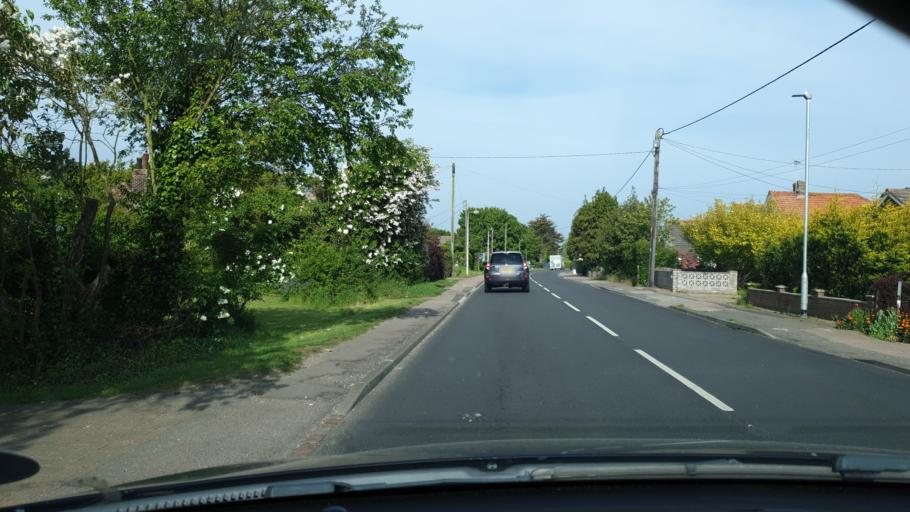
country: GB
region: England
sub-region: Essex
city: Frinton-on-Sea
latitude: 51.8446
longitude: 1.2056
